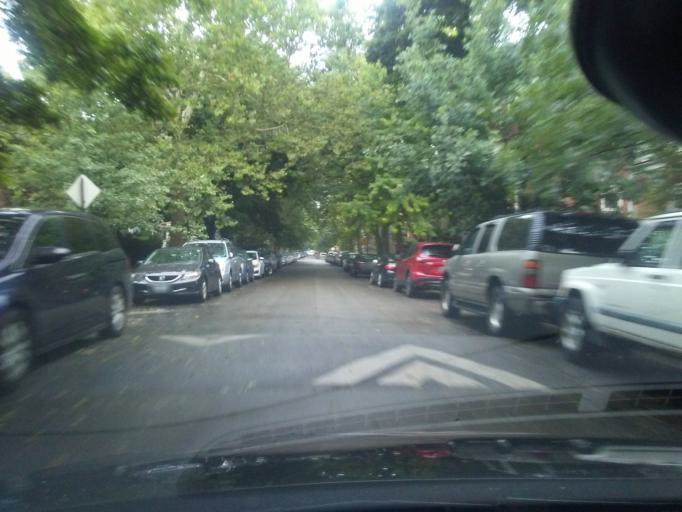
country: US
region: Illinois
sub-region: Cook County
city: Evanston
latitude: 41.9936
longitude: -87.6636
